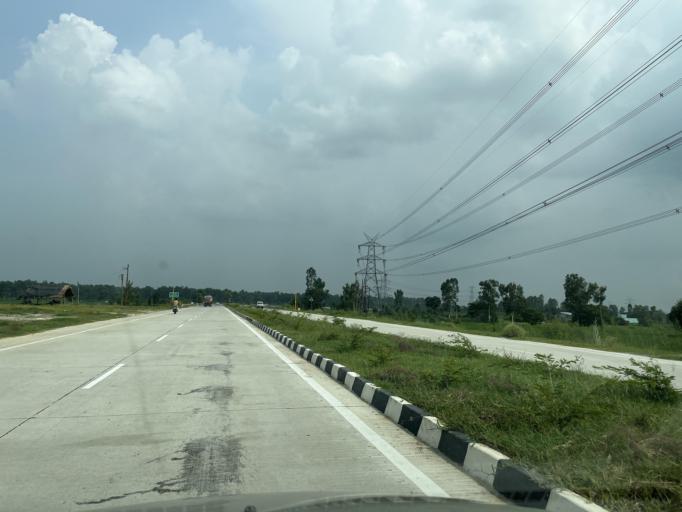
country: IN
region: Uttarakhand
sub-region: Udham Singh Nagar
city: Jaspur
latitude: 29.2819
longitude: 78.8627
